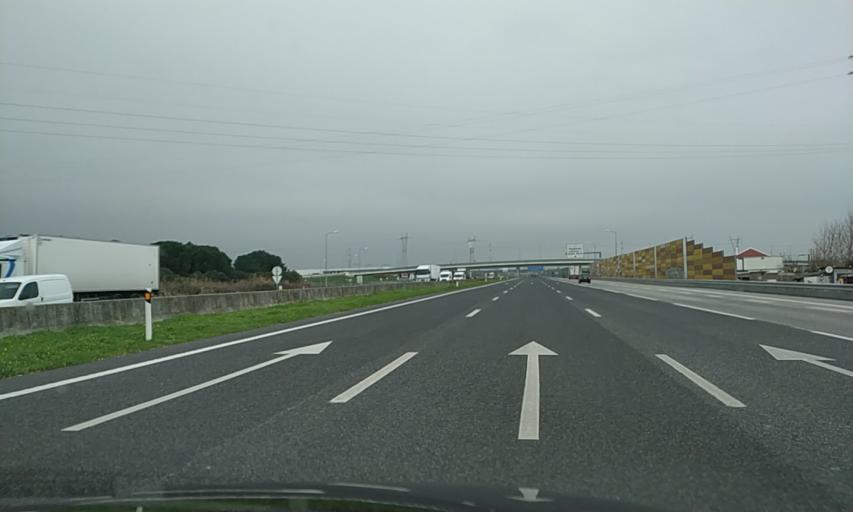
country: PT
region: Lisbon
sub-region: Vila Franca de Xira
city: Castanheira do Ribatejo
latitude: 39.0024
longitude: -8.9671
